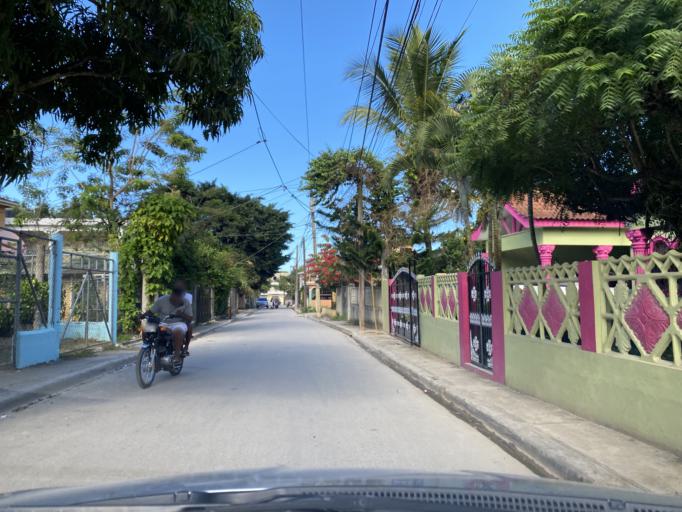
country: DO
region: Samana
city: Las Terrenas
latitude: 19.3074
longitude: -69.5431
